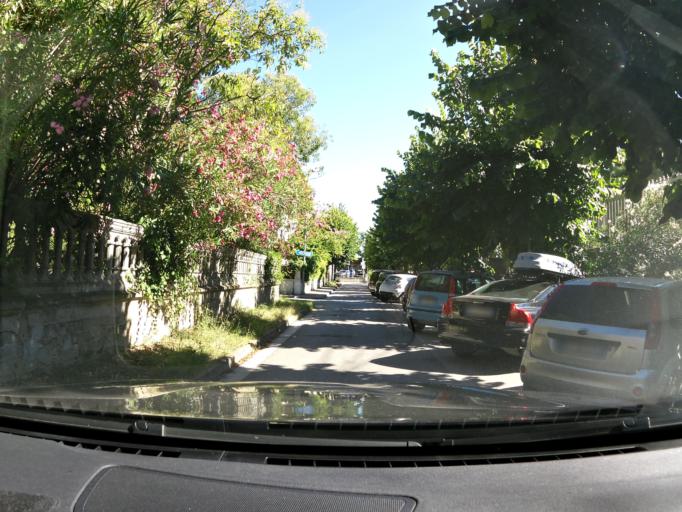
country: IT
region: The Marches
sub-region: Province of Fermo
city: Porto San Giorgio
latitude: 43.1819
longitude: 13.7965
